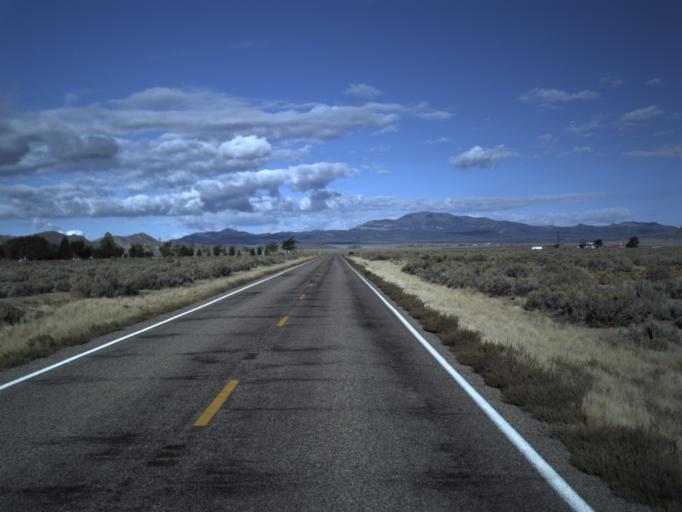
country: US
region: Utah
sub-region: Beaver County
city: Milford
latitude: 38.4037
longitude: -113.0430
